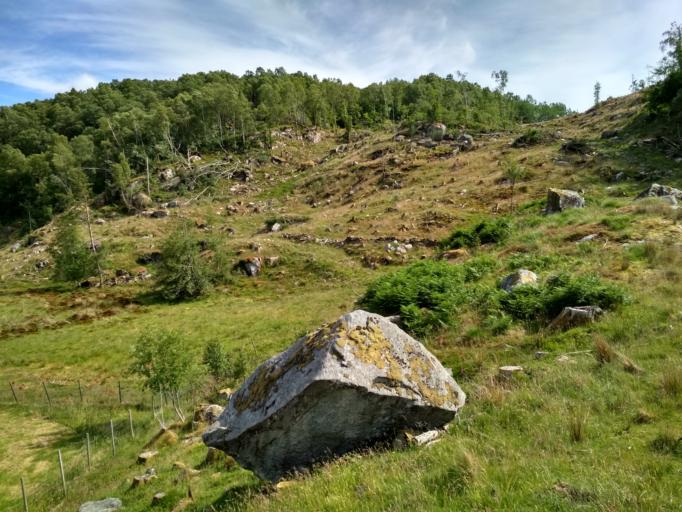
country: NO
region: Rogaland
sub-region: Finnoy
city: Judaberg
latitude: 59.2647
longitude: 5.8577
